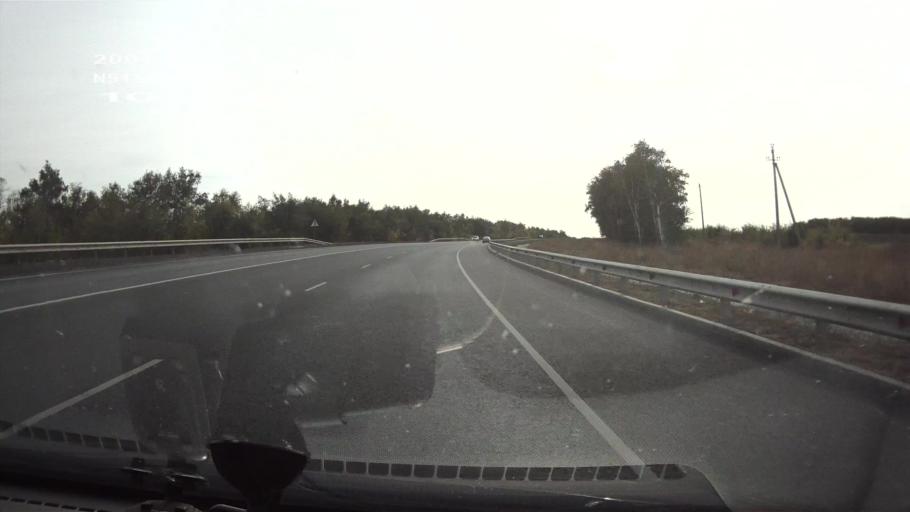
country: RU
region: Saratov
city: Sinodskoye
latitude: 51.9031
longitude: 46.5464
